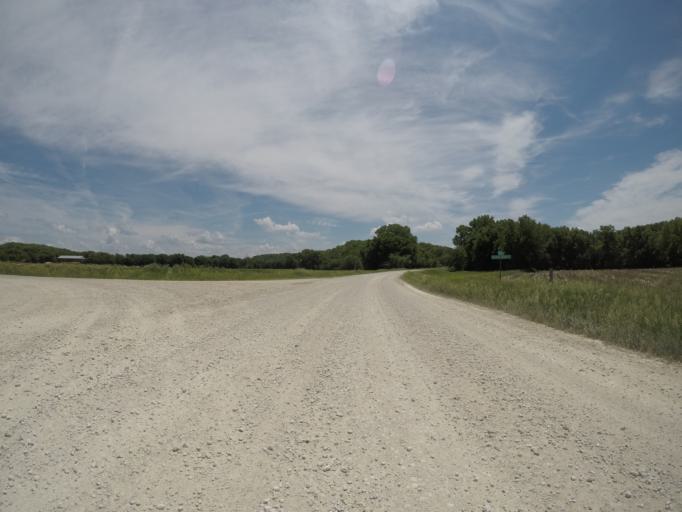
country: US
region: Kansas
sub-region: Wabaunsee County
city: Alma
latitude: 38.9510
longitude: -96.2431
